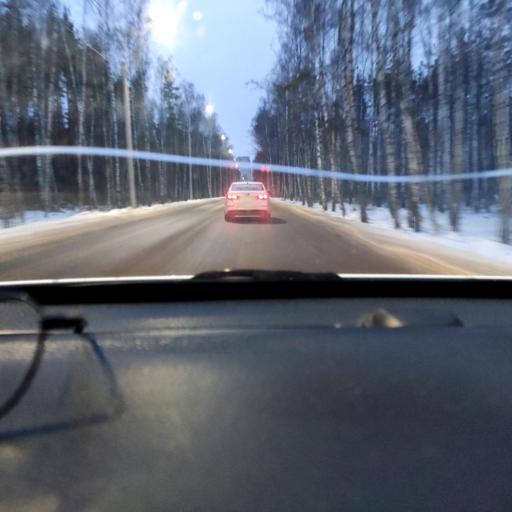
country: RU
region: Voronezj
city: Somovo
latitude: 51.6993
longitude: 39.2820
